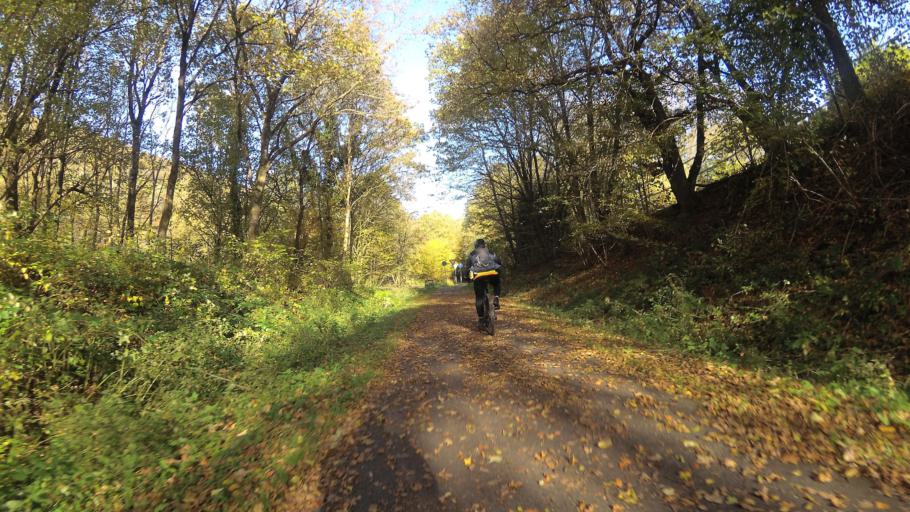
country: DE
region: Rheinland-Pfalz
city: Morscheid
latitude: 49.7355
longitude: 6.7427
